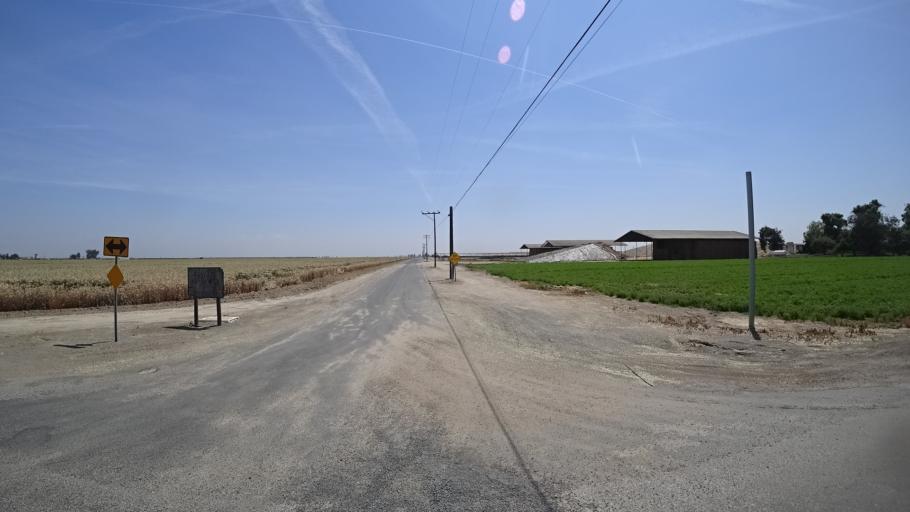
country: US
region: California
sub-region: Tulare County
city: London
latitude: 36.4014
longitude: -119.5288
